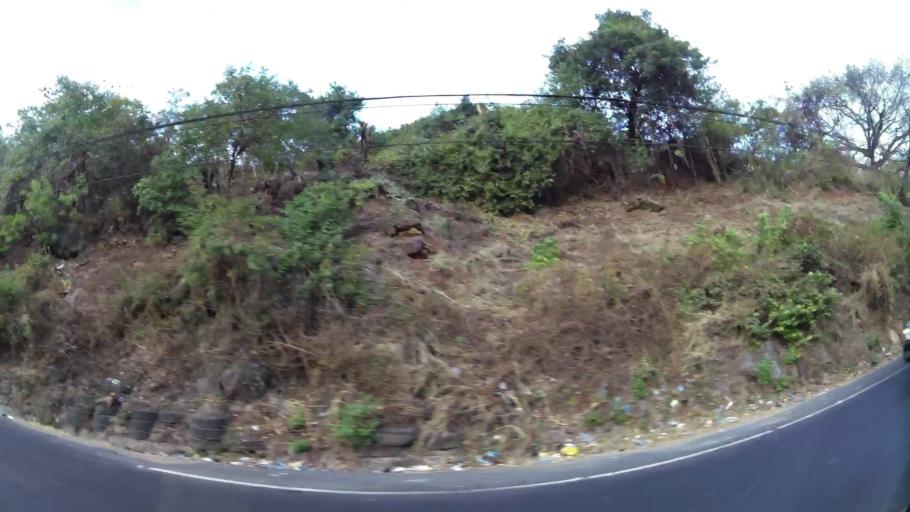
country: SV
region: San Vicente
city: Apastepeque
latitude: 13.6494
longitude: -88.7837
